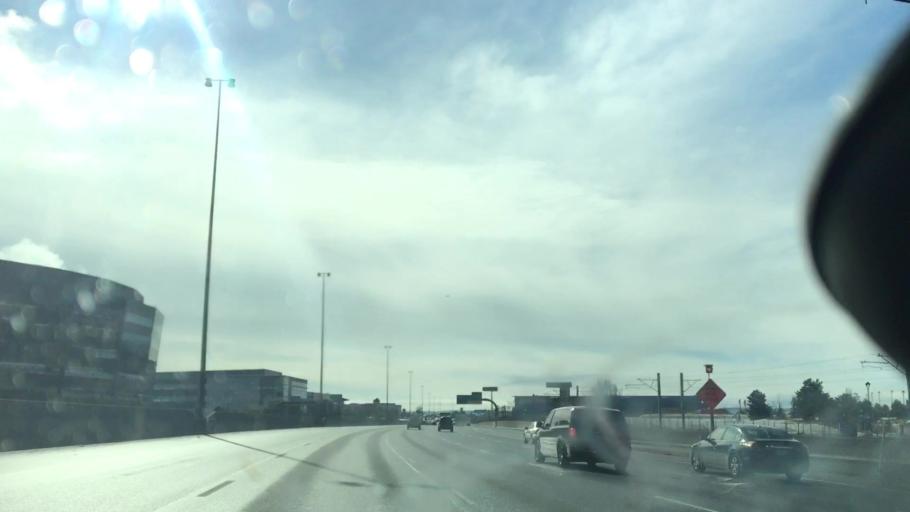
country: US
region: Colorado
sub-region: Arapahoe County
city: Centennial
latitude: 39.5784
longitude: -104.8757
